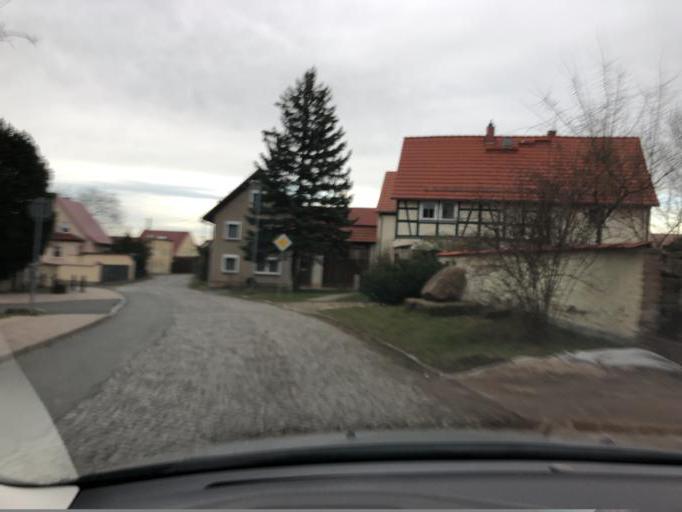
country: DE
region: Thuringia
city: Monchenholzhausen
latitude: 50.9519
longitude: 11.1482
